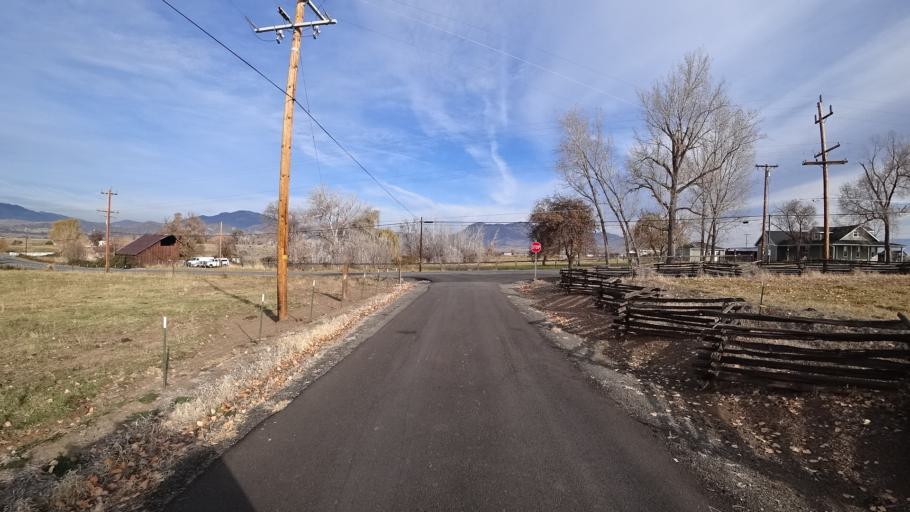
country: US
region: California
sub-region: Siskiyou County
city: Montague
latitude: 41.7305
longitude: -122.5785
